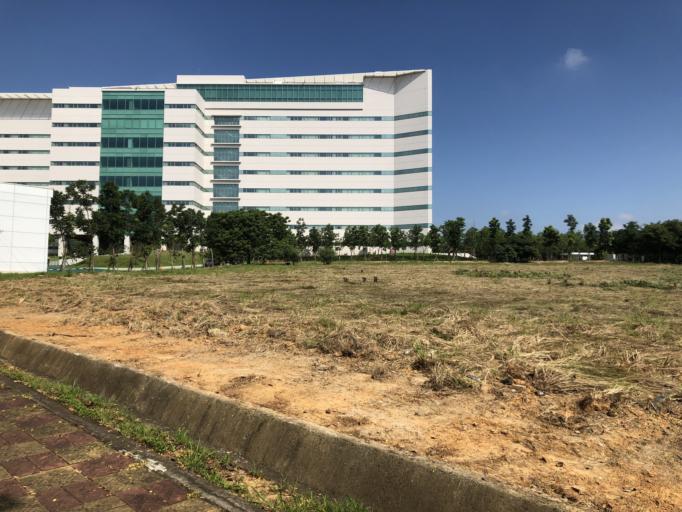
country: TW
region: Taiwan
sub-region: Taichung City
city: Taichung
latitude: 24.1480
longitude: 120.6062
